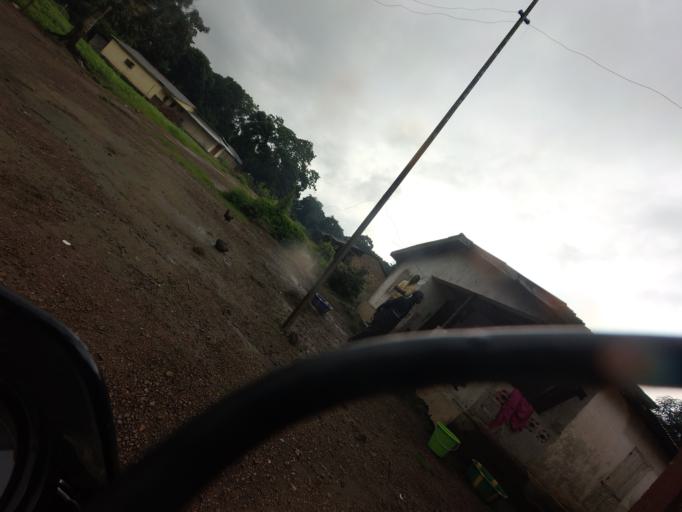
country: SL
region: Northern Province
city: Kukuna
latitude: 9.2879
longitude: -12.6716
